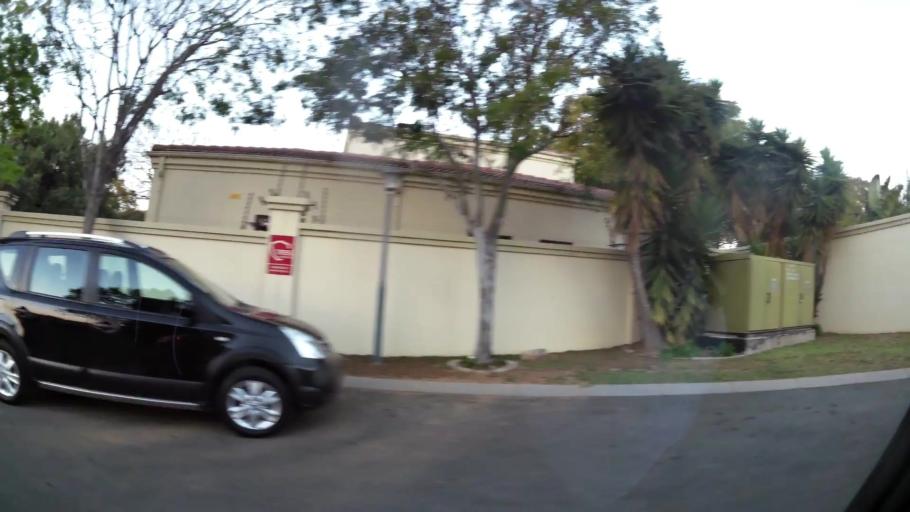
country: ZA
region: Gauteng
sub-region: City of Johannesburg Metropolitan Municipality
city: Diepsloot
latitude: -26.0298
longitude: 28.0207
